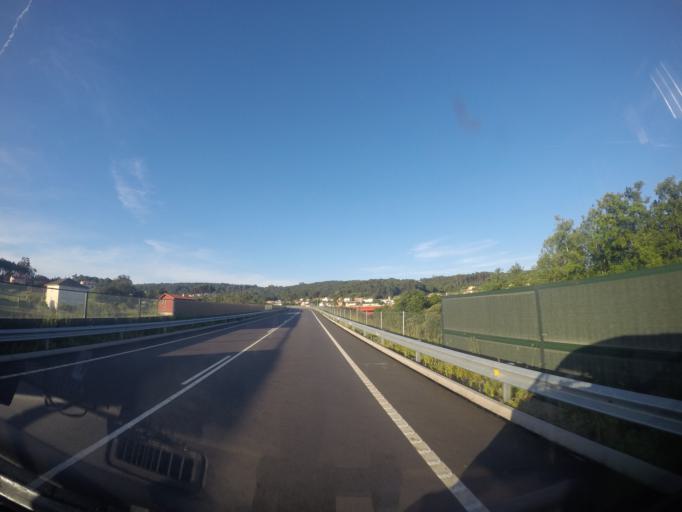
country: ES
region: Galicia
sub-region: Provincia da Coruna
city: Noia
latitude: 42.7975
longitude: -8.8911
